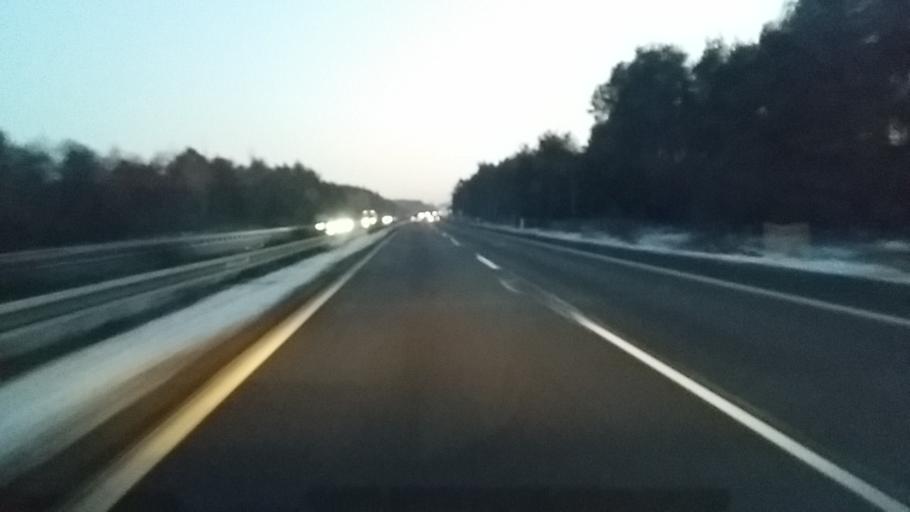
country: CZ
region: South Moravian
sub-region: Okres Breclav
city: Lanzhot
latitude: 48.6279
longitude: 17.0078
